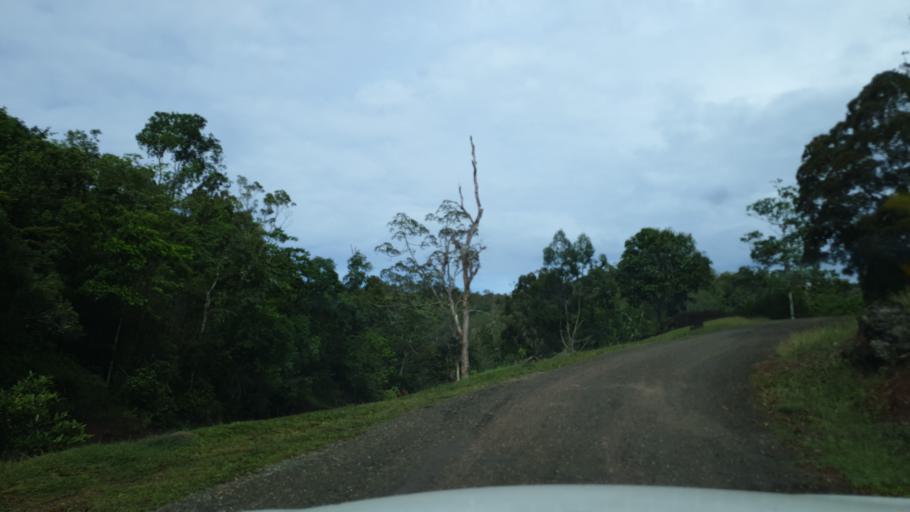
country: PG
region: National Capital
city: Port Moresby
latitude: -9.4361
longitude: 147.3940
